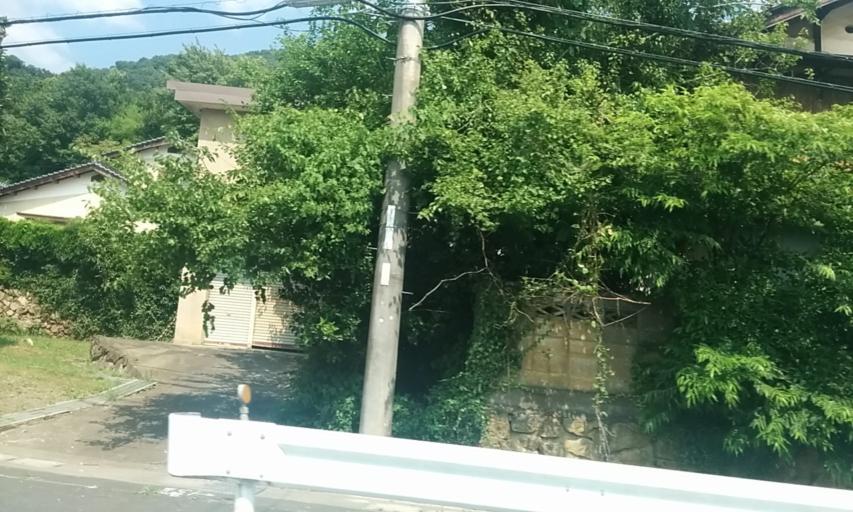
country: JP
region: Kyoto
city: Fukuchiyama
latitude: 35.3291
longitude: 135.1198
